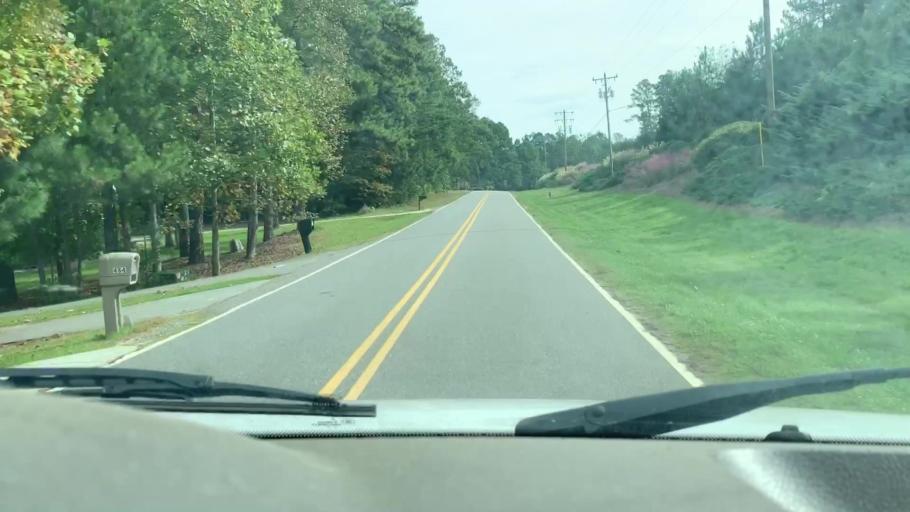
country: US
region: North Carolina
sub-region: Catawba County
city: Lake Norman of Catawba
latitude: 35.5730
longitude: -80.9402
